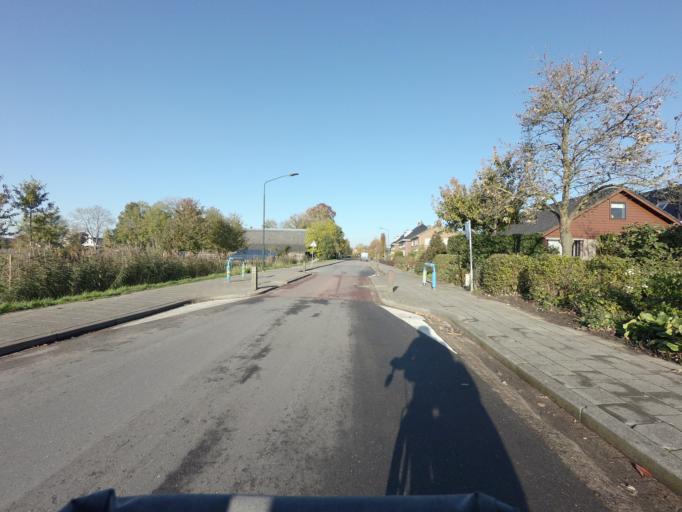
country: NL
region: North Brabant
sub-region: Gemeente Woudrichem
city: Woudrichem
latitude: 51.7823
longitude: 5.0534
